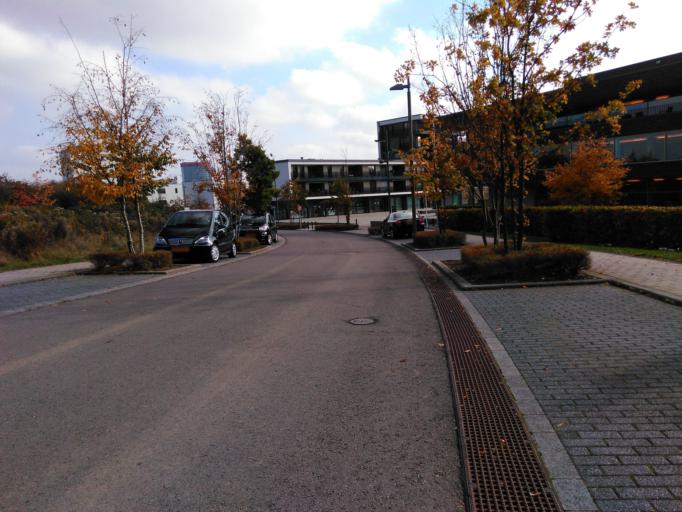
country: LU
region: Luxembourg
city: Belvaux
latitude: 49.5091
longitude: 5.9339
